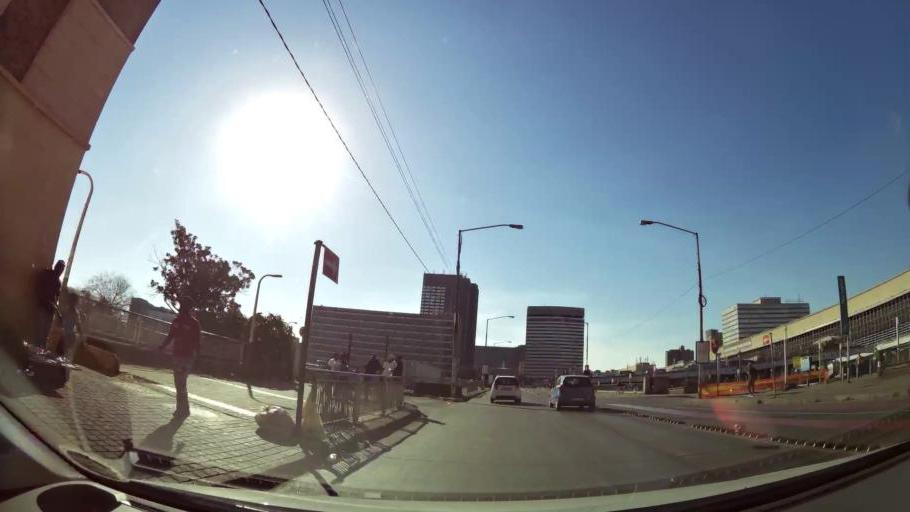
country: ZA
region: Gauteng
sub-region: City of Johannesburg Metropolitan Municipality
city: Johannesburg
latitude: -26.1987
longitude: 28.0412
